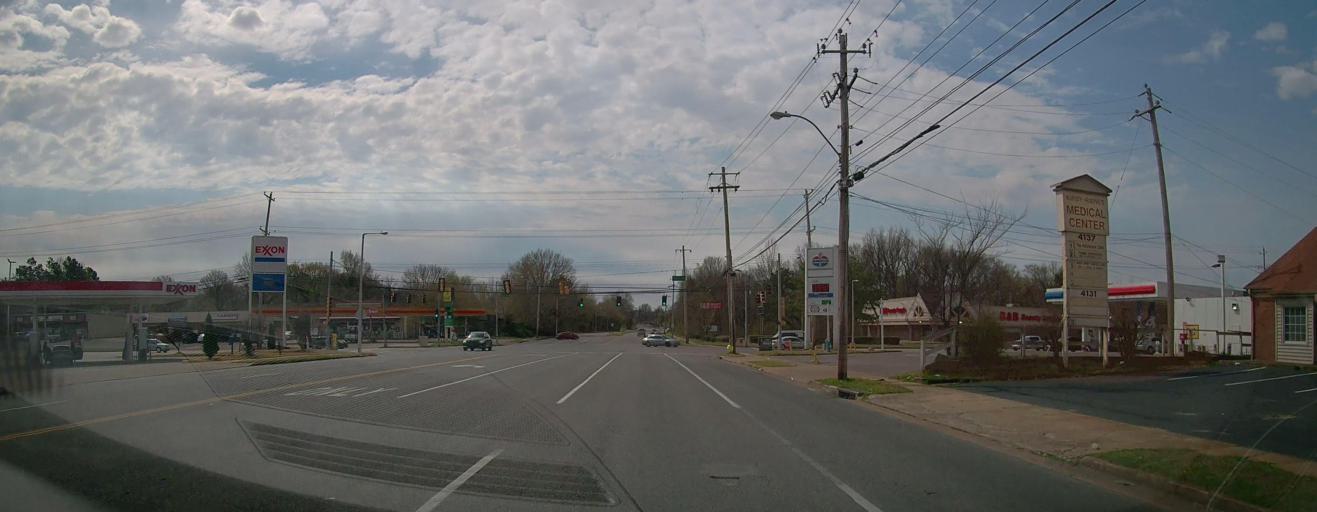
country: US
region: Tennessee
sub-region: Shelby County
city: Germantown
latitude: 35.0355
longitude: -89.8477
